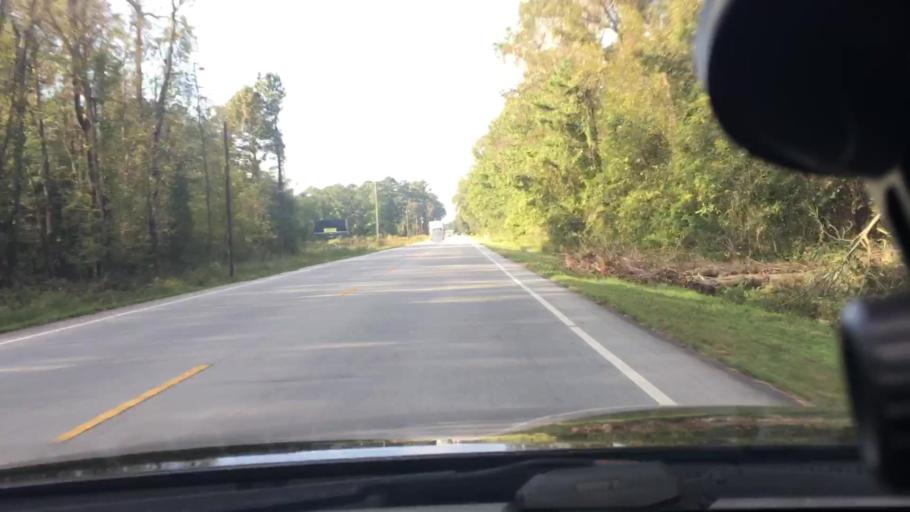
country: US
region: North Carolina
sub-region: Craven County
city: New Bern
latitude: 35.2095
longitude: -77.0608
